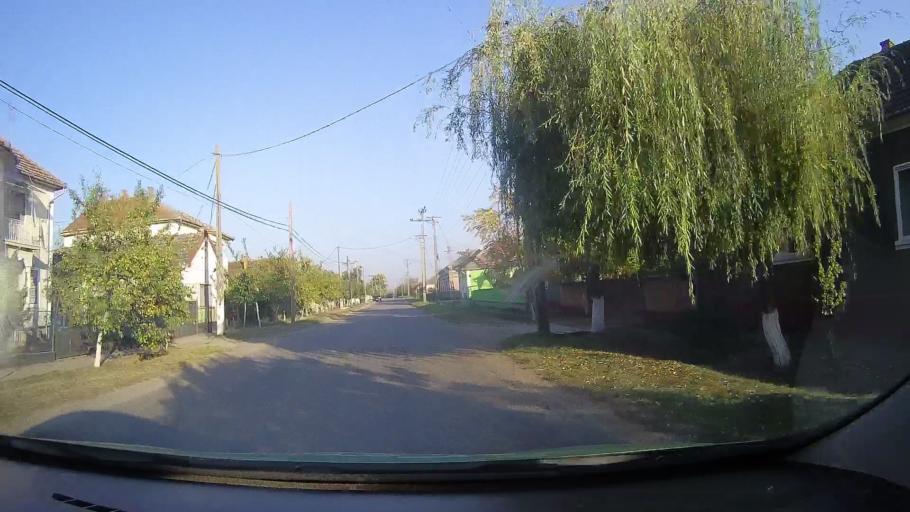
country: RO
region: Arad
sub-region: Comuna Tarnova
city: Tarnova
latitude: 46.3188
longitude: 21.7968
